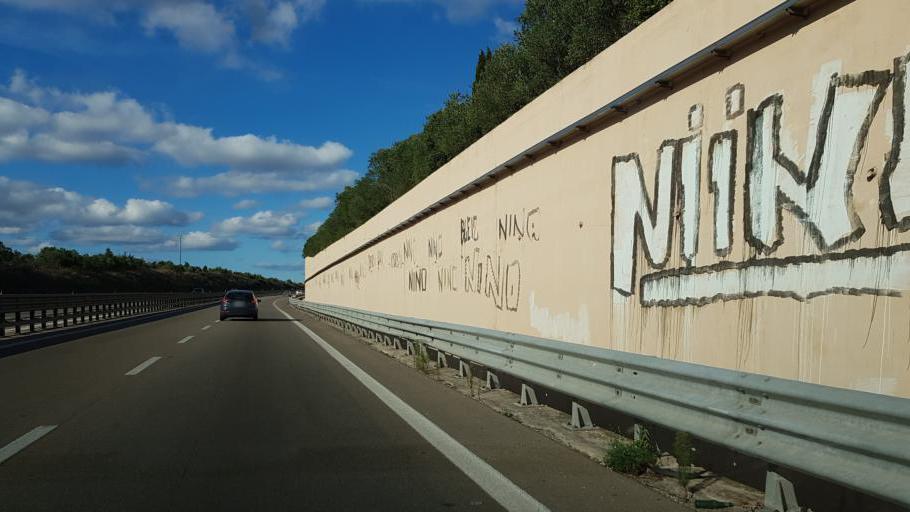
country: IT
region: Apulia
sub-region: Provincia di Lecce
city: Arnesano
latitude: 40.3450
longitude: 18.1253
